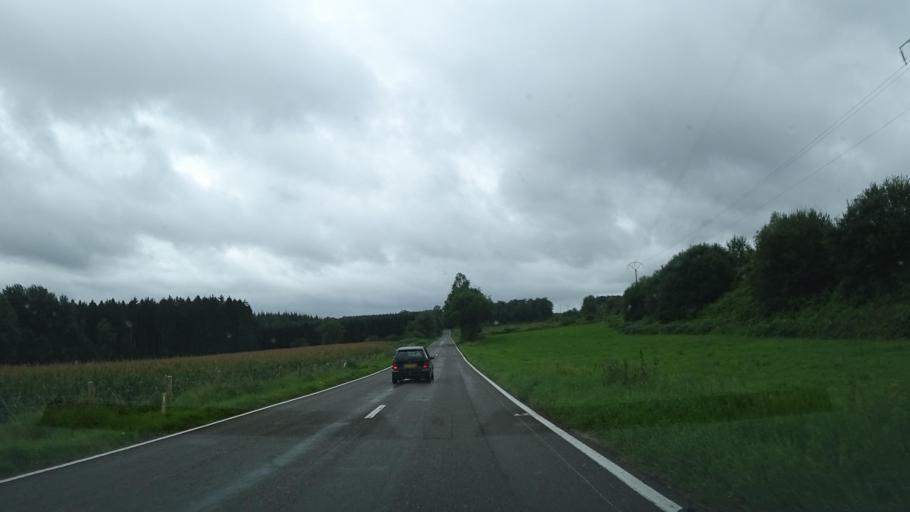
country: BE
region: Wallonia
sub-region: Province du Luxembourg
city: Chiny
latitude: 49.7940
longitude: 5.3305
